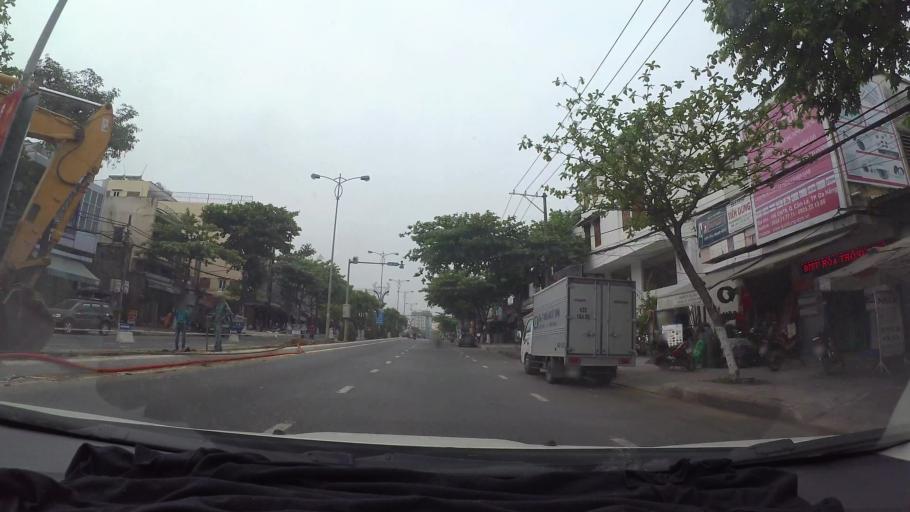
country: VN
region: Da Nang
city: Cam Le
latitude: 16.0219
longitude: 108.2132
